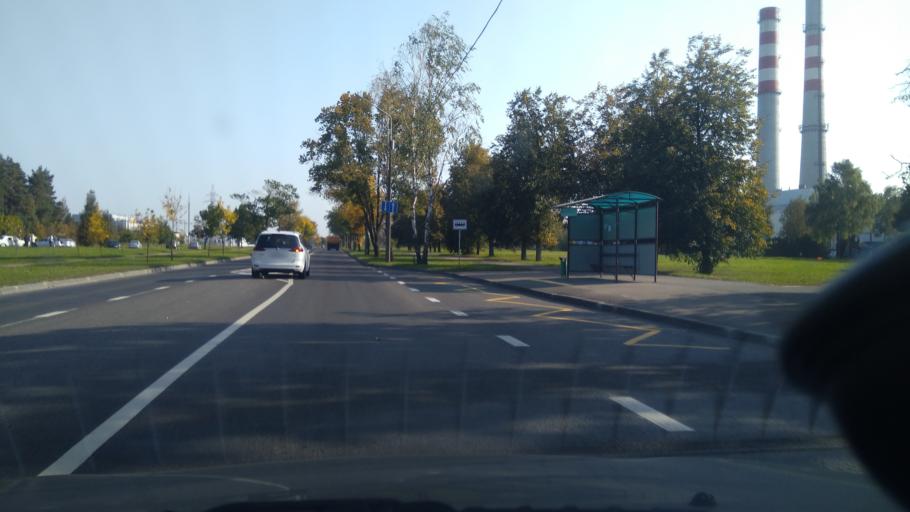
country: BY
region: Minsk
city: Vyaliki Trastsyanets
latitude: 53.8289
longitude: 27.7005
